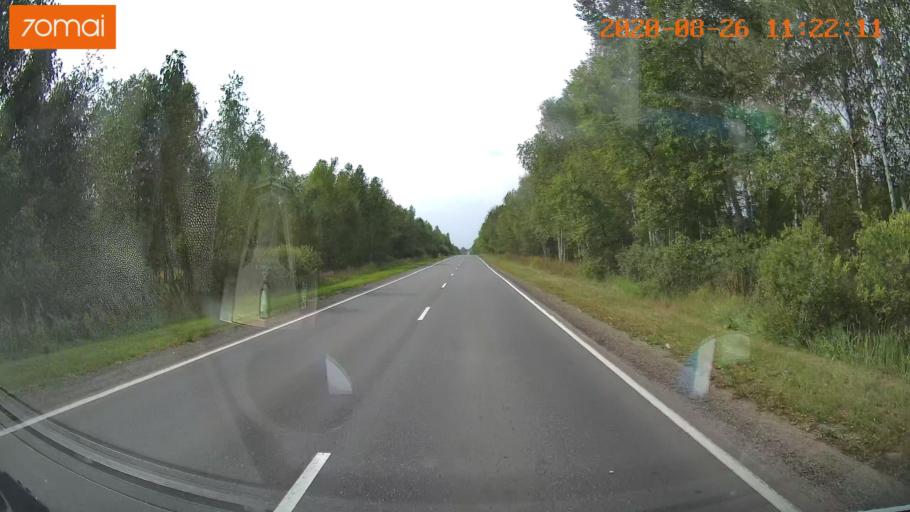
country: RU
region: Rjazan
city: Shilovo
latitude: 54.3670
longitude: 41.0316
